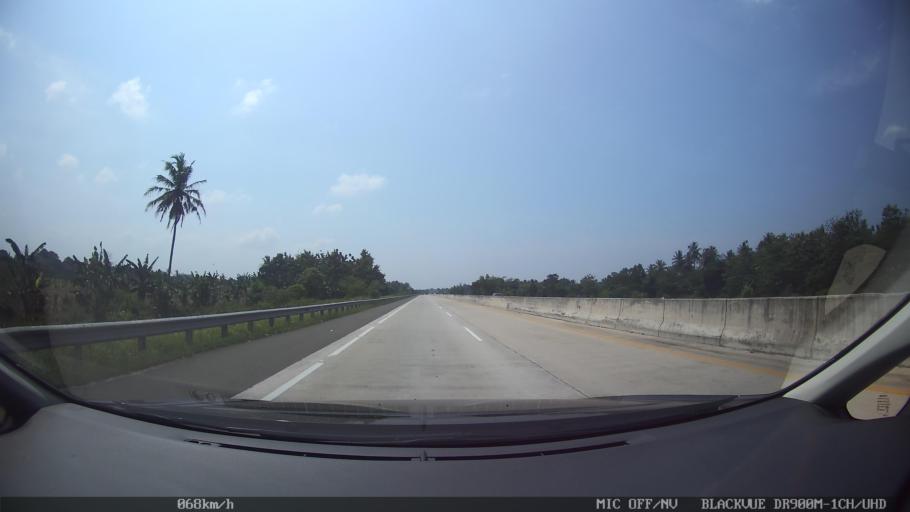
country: ID
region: Lampung
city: Natar
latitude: -5.3069
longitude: 105.2487
